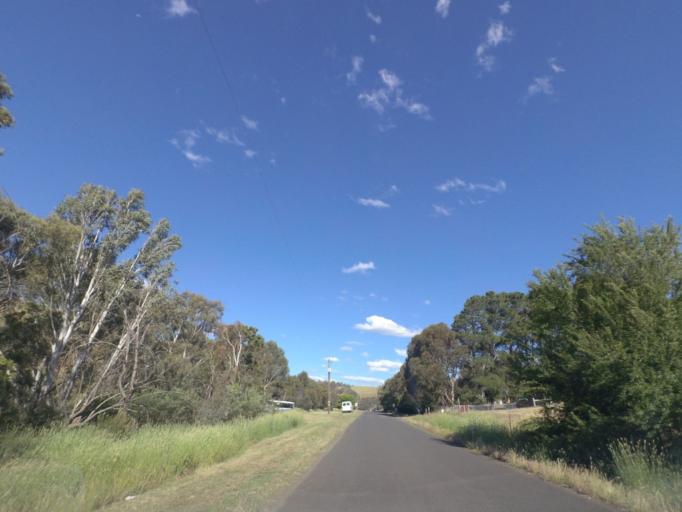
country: AU
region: Victoria
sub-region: Hume
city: Craigieburn
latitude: -37.4040
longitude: 144.8985
